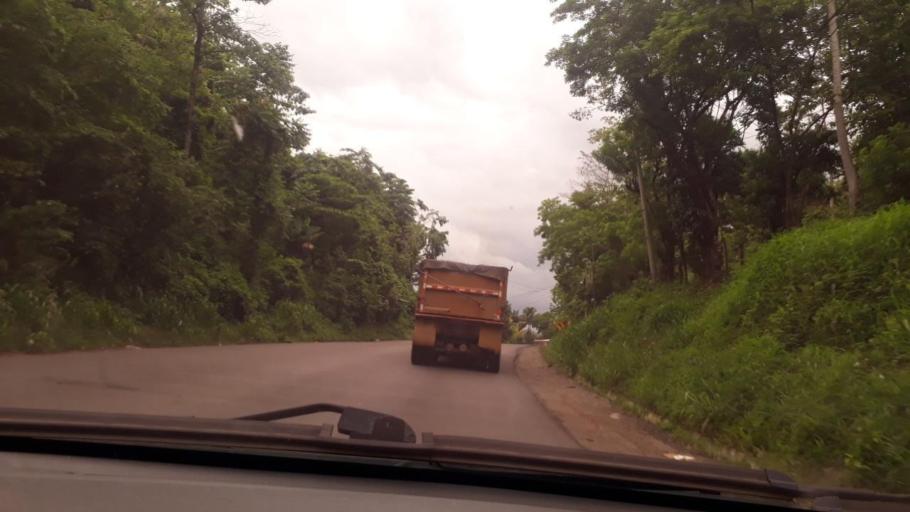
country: GT
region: Izabal
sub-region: Municipio de Los Amates
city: Los Amates
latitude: 15.2678
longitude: -89.0863
